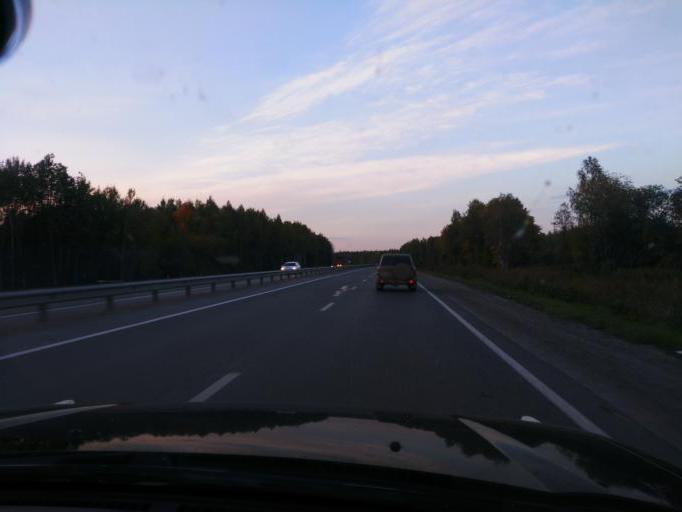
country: RU
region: Perm
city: Polazna
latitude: 58.2298
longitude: 56.4253
